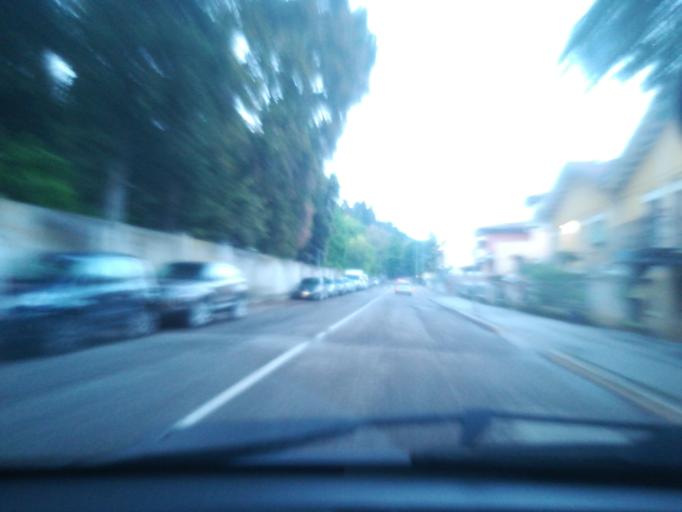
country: IT
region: The Marches
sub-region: Provincia di Macerata
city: Villa Potenza
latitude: 43.2948
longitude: 13.4230
